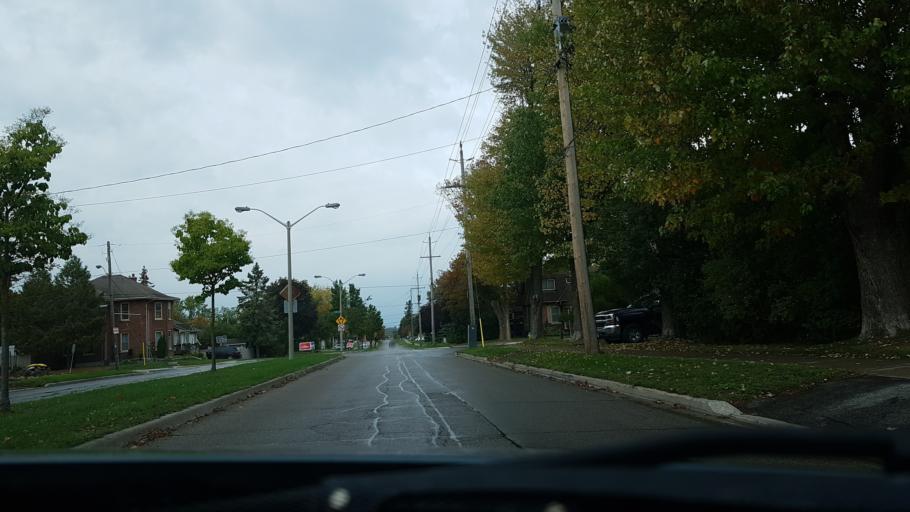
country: CA
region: Ontario
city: Omemee
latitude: 44.3617
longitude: -78.7443
